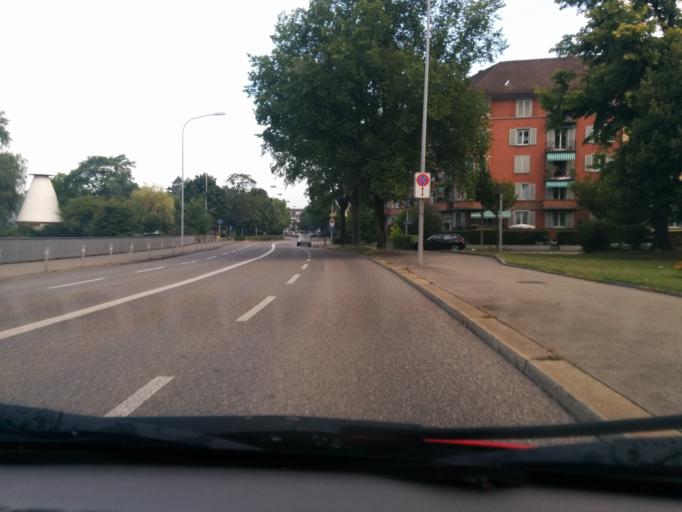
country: CH
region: Zurich
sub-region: Bezirk Zuerich
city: Zuerich (Kreis 8)
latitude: 47.3513
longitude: 8.5596
